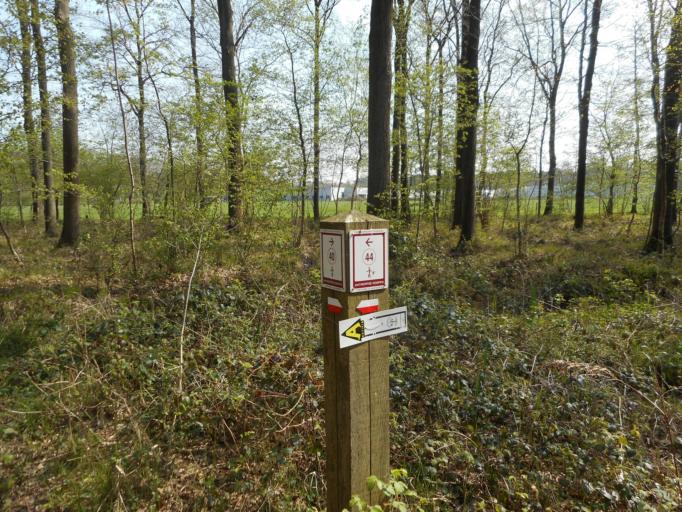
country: BE
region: Flanders
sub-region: Provincie Antwerpen
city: Zoersel
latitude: 51.2508
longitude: 4.7009
